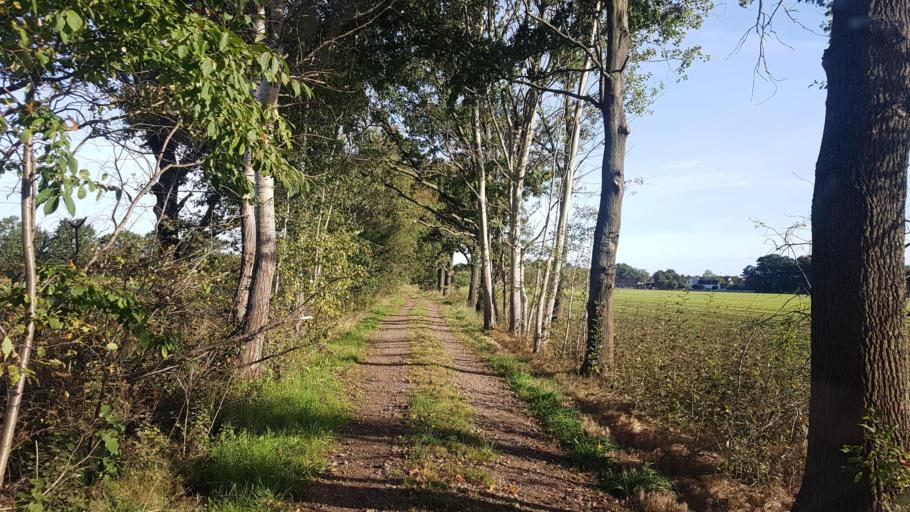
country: DE
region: Brandenburg
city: Tettau
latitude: 51.4293
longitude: 13.7174
